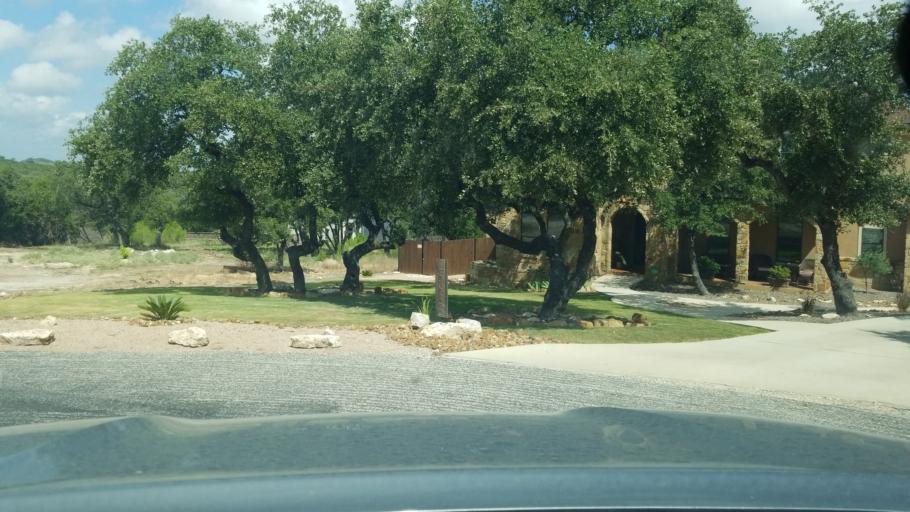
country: US
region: Texas
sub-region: Bexar County
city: Timberwood Park
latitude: 29.6858
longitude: -98.5204
